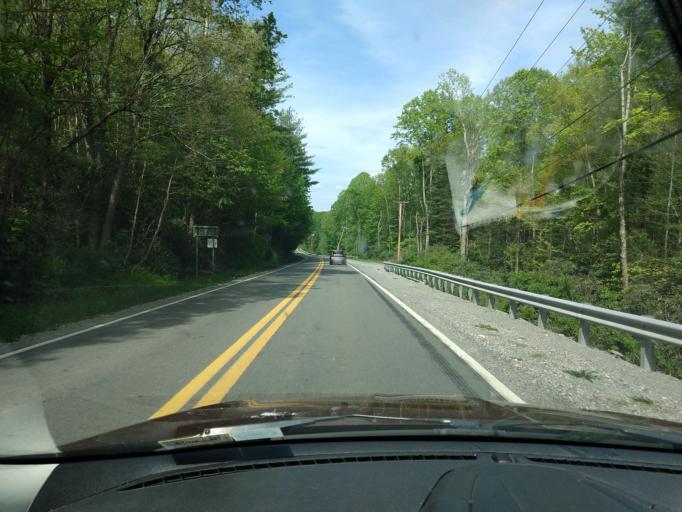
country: US
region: West Virginia
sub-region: Raleigh County
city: Daniels
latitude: 37.7781
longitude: -81.1168
